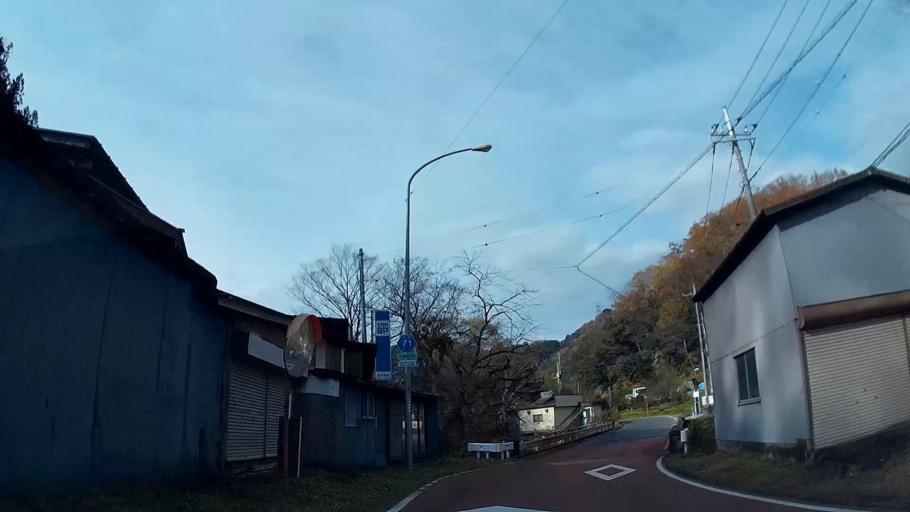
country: JP
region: Saitama
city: Chichibu
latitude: 36.0587
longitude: 138.9758
